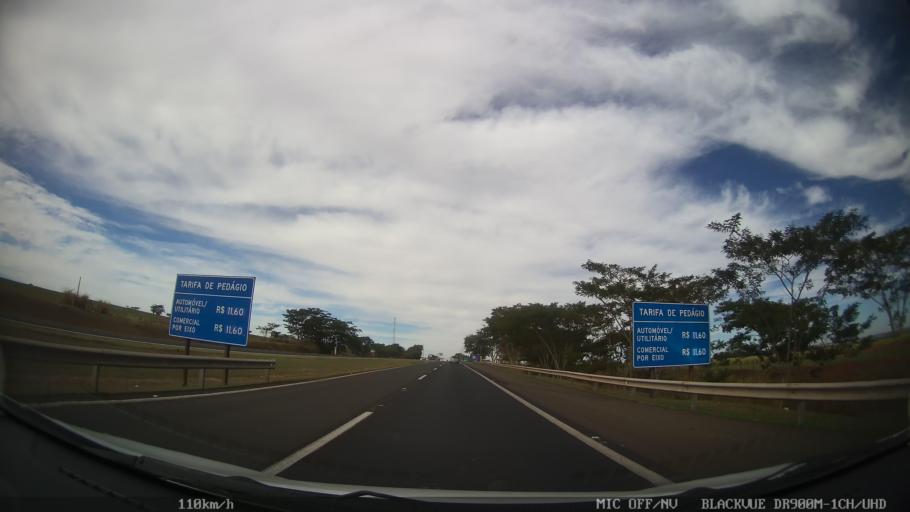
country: BR
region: Sao Paulo
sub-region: Santa Adelia
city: Santa Adelia
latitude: -21.3796
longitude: -48.7373
